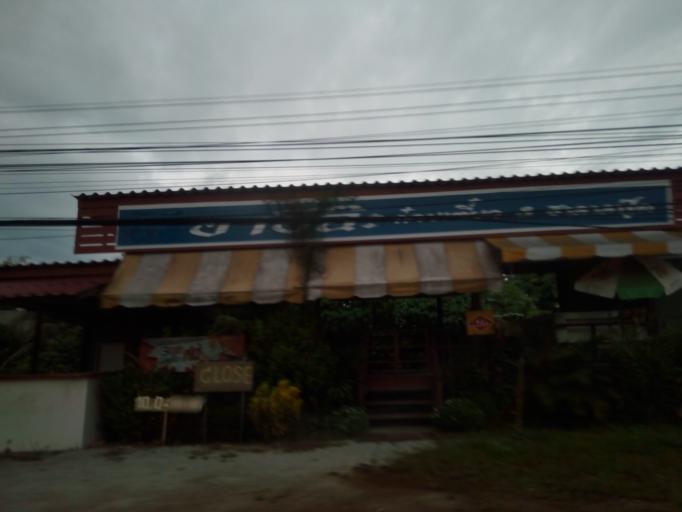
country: TH
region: Phuket
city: Thalang
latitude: 8.0542
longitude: 98.4085
